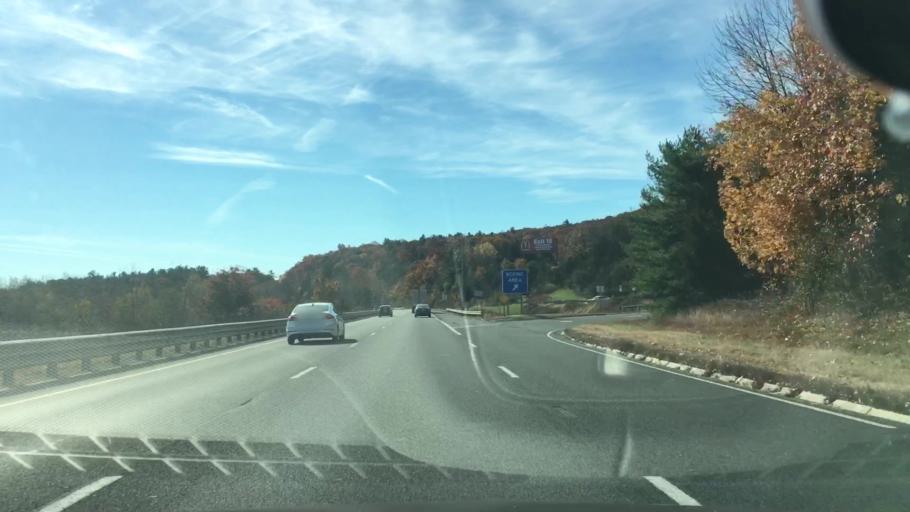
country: US
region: Massachusetts
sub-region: Hampshire County
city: South Hadley
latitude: 42.2551
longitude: -72.6201
